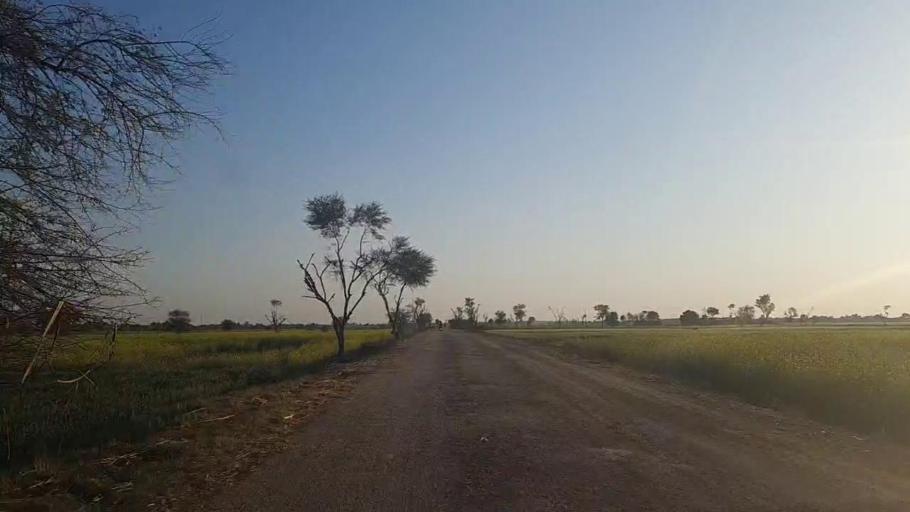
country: PK
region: Sindh
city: Jam Sahib
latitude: 26.3411
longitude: 68.6959
